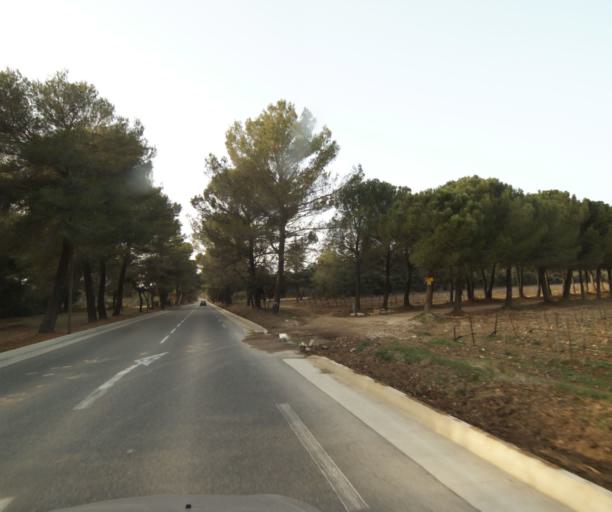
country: FR
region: Provence-Alpes-Cote d'Azur
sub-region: Departement des Bouches-du-Rhone
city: Eguilles
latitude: 43.6138
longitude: 5.3623
